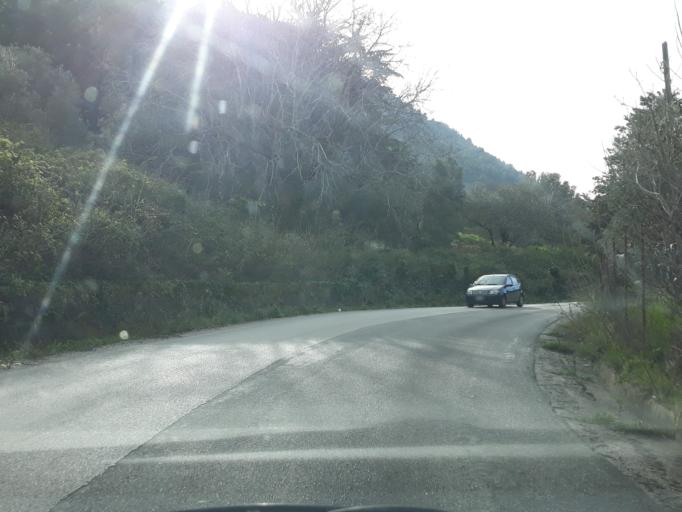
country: IT
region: Sicily
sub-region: Palermo
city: Piano Maglio-Blandino
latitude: 38.0400
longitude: 13.3140
